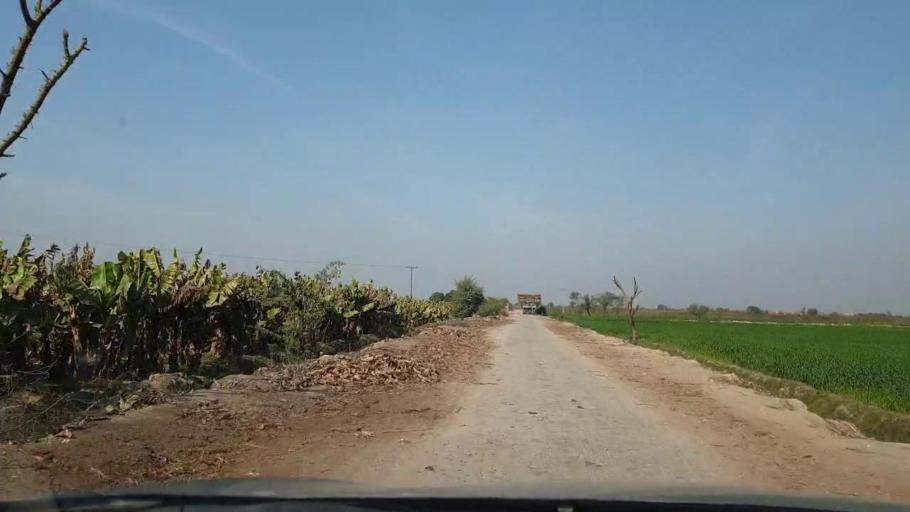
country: PK
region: Sindh
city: Berani
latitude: 25.6923
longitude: 68.7535
